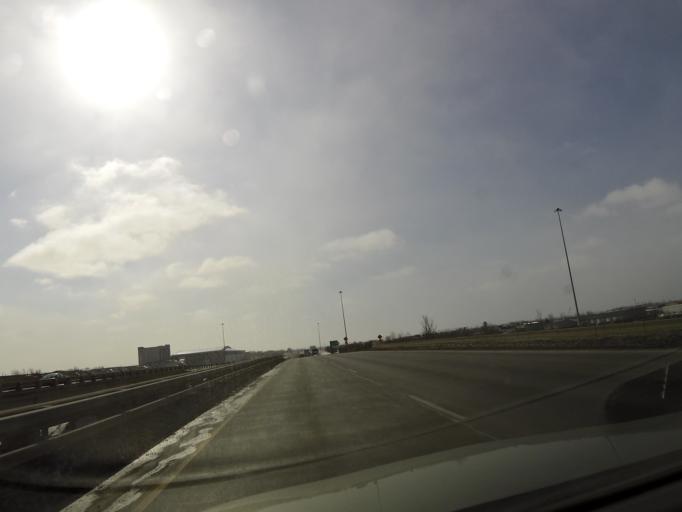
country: US
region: North Dakota
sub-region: Grand Forks County
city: Grand Forks
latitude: 47.9189
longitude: -97.0937
